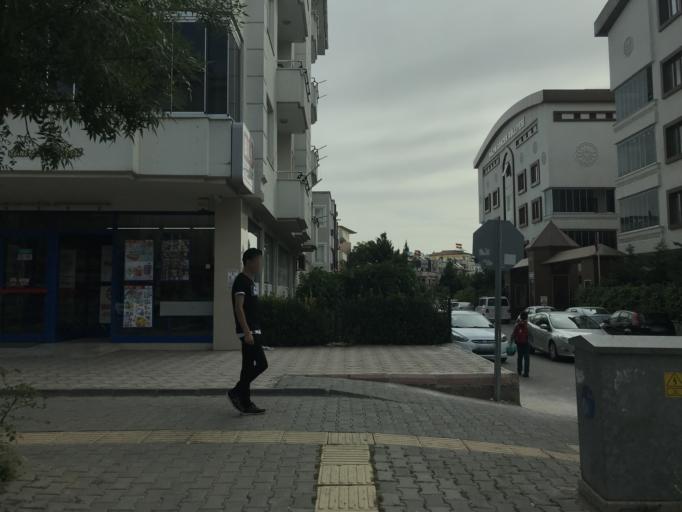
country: TR
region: Gaziantep
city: Sahinbey
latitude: 37.0550
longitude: 37.3324
